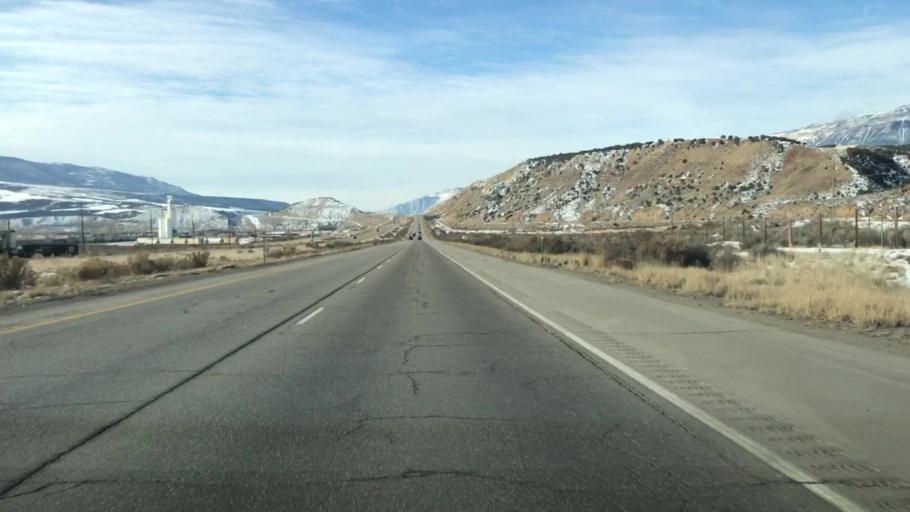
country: US
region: Colorado
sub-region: Garfield County
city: Rifle
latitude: 39.5108
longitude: -107.8698
